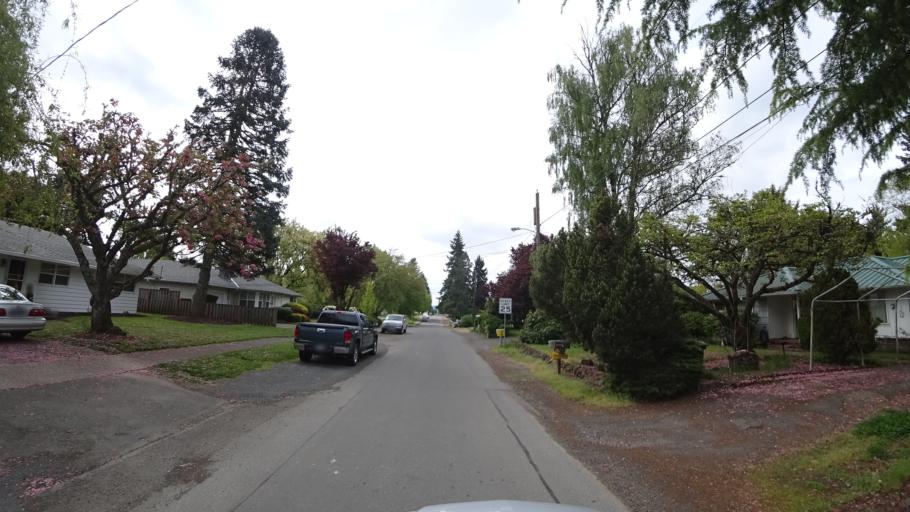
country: US
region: Oregon
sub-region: Washington County
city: Hillsboro
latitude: 45.5277
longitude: -122.9962
